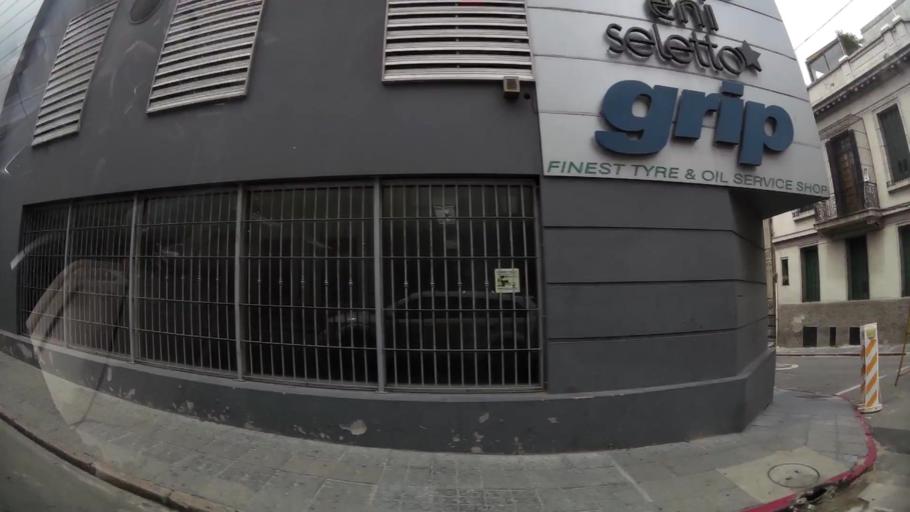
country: UY
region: Montevideo
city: Montevideo
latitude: -34.9084
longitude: -56.2044
